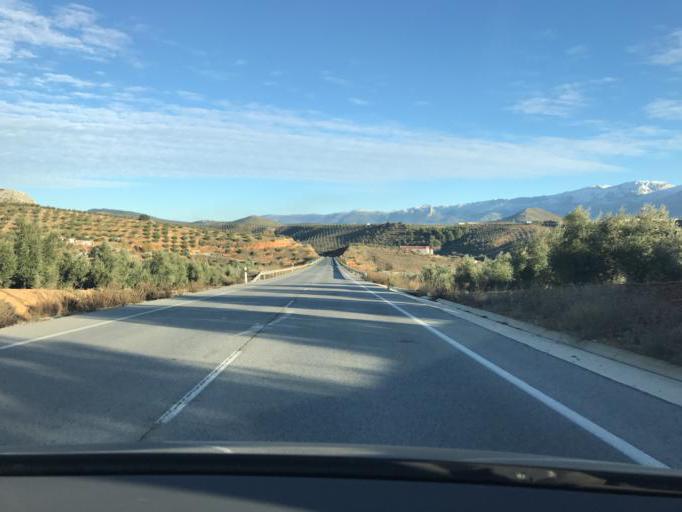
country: ES
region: Andalusia
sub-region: Provincia de Granada
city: Iznalloz
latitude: 37.4022
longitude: -3.5312
